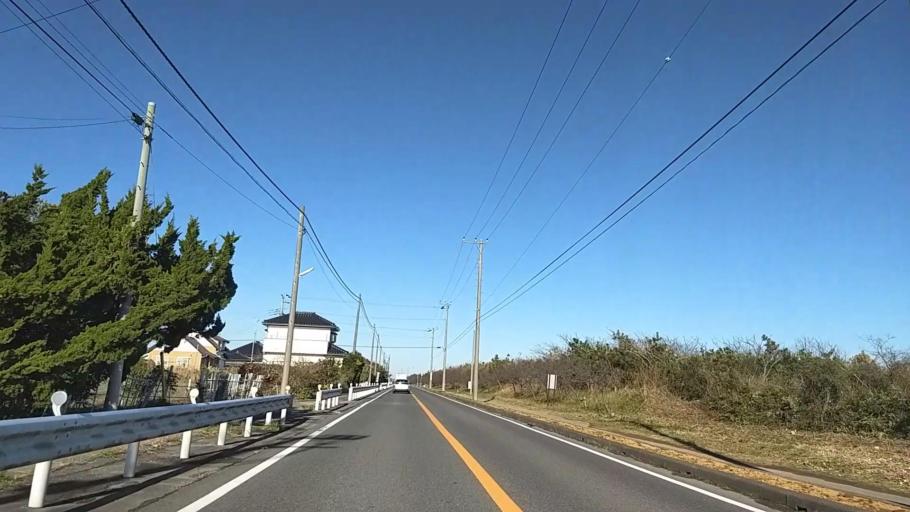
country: JP
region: Chiba
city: Togane
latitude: 35.4640
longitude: 140.4091
